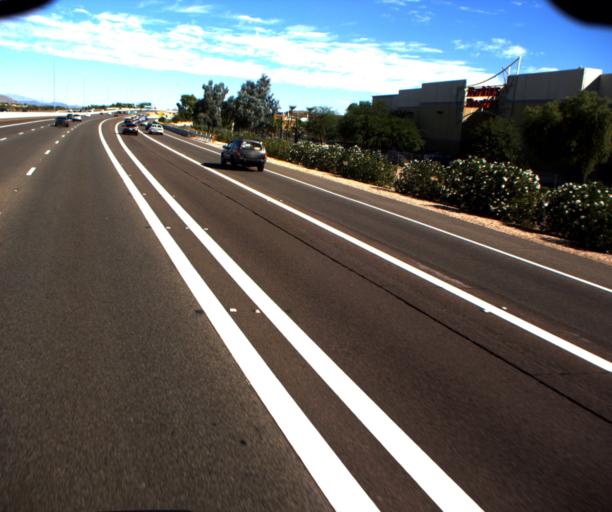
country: US
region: Arizona
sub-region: Maricopa County
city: Sun City
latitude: 33.6299
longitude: -112.2400
